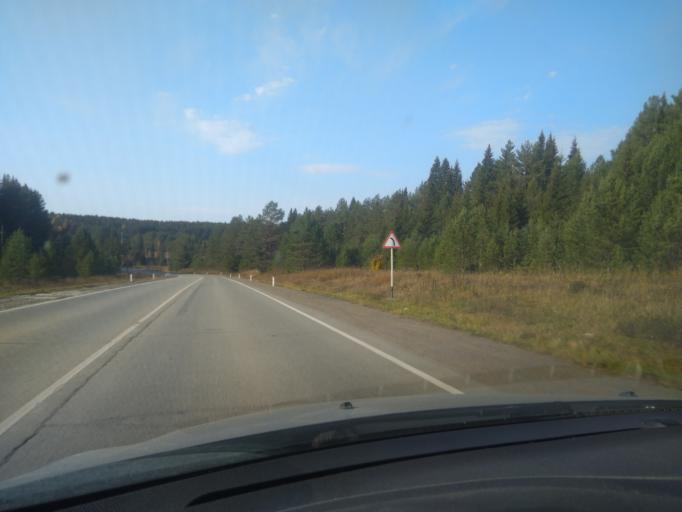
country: RU
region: Sverdlovsk
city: Nizhniye Sergi
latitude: 56.6478
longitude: 59.2590
